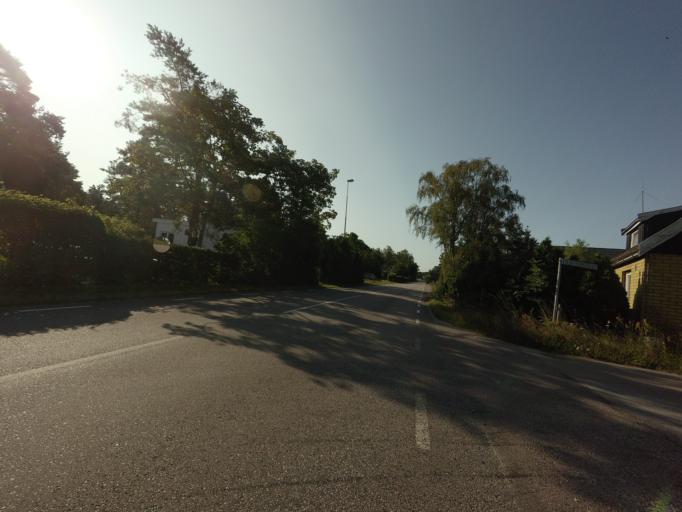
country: SE
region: Skane
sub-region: Kavlinge Kommun
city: Hofterup
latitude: 55.8305
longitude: 12.9639
